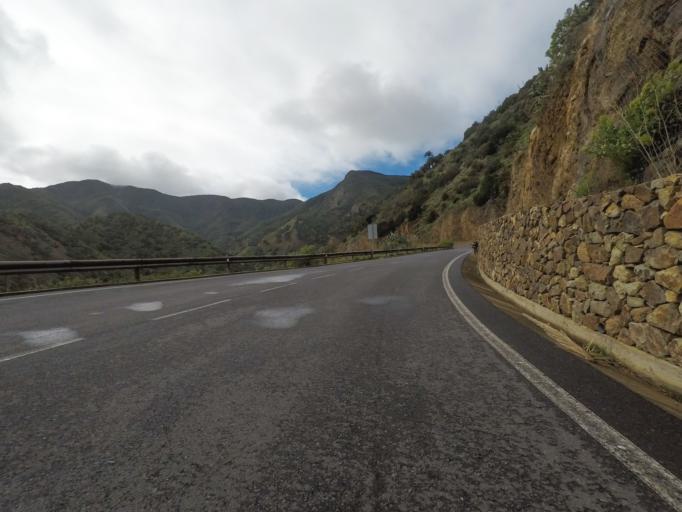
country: ES
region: Canary Islands
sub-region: Provincia de Santa Cruz de Tenerife
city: Vallehermosa
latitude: 28.1663
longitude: -17.2779
